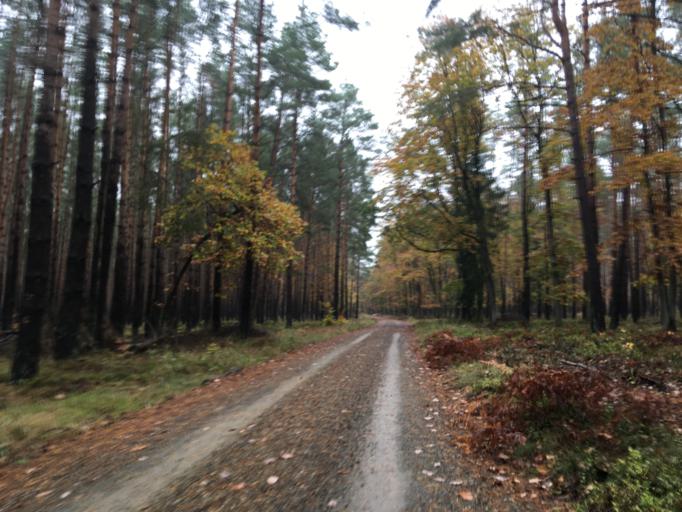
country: DE
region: Brandenburg
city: Briesen
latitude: 52.2546
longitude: 14.2928
